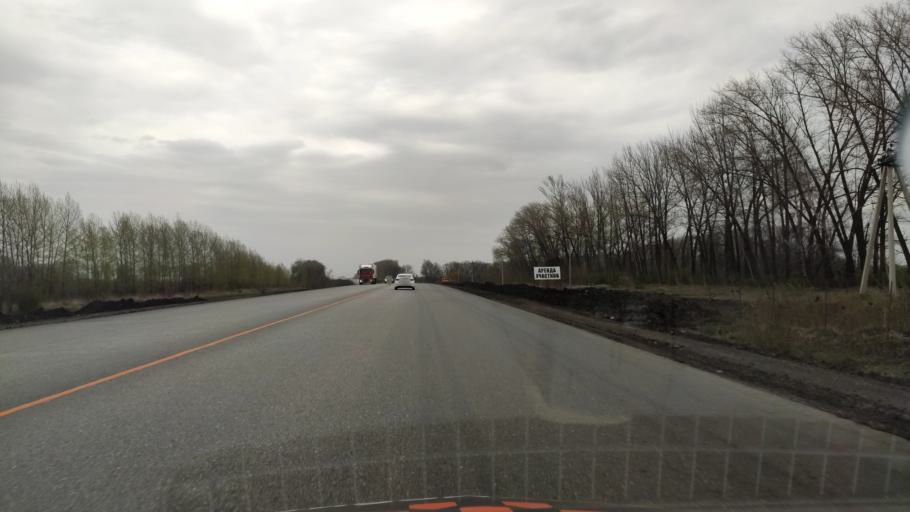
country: RU
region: Kursk
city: Gorshechnoye
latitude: 51.5474
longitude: 38.0608
